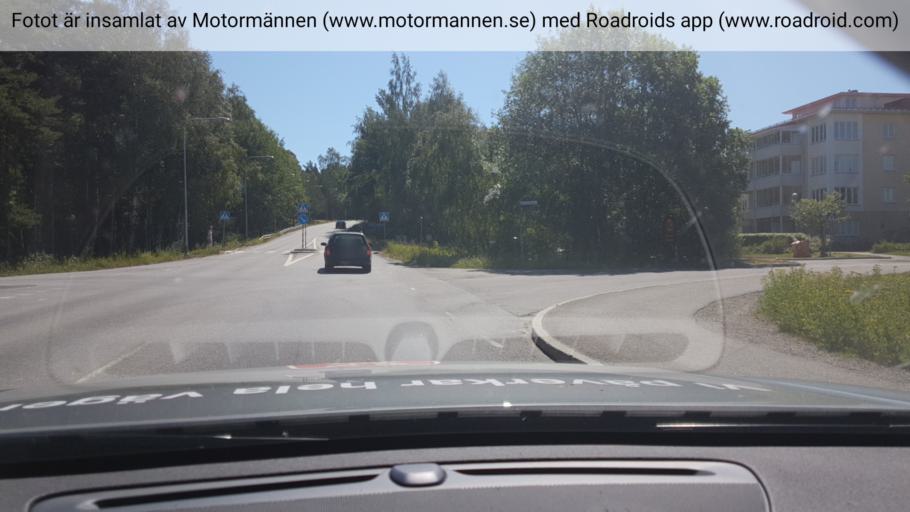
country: SE
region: Stockholm
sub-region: Haninge Kommun
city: Haninge
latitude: 59.1902
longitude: 18.1799
